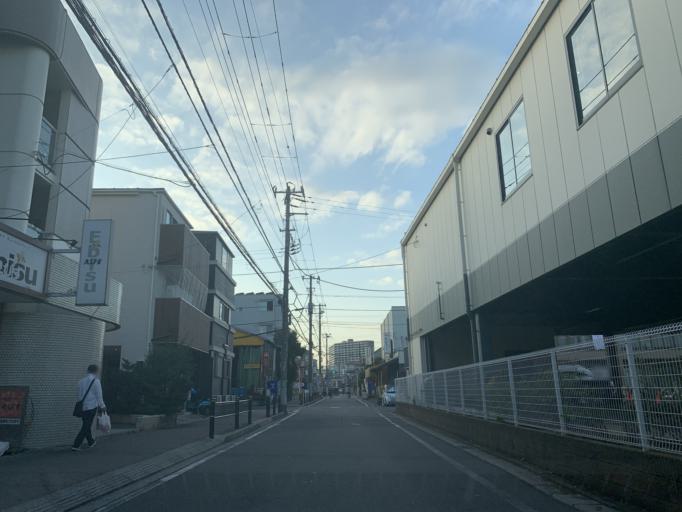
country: JP
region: Tokyo
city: Urayasu
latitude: 35.6727
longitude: 139.8953
